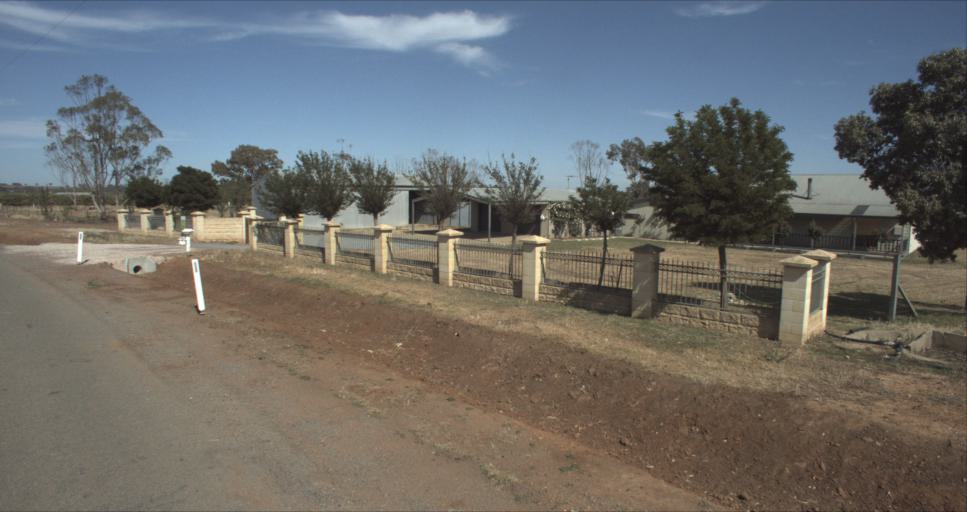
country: AU
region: New South Wales
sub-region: Leeton
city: Leeton
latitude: -34.5773
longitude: 146.4796
